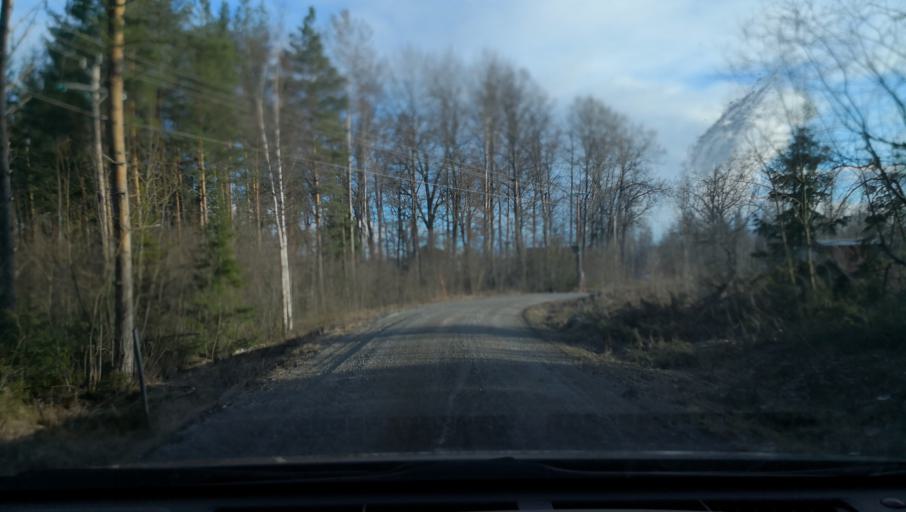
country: SE
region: Vaestmanland
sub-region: Arboga Kommun
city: Arboga
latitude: 59.4167
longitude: 15.7447
